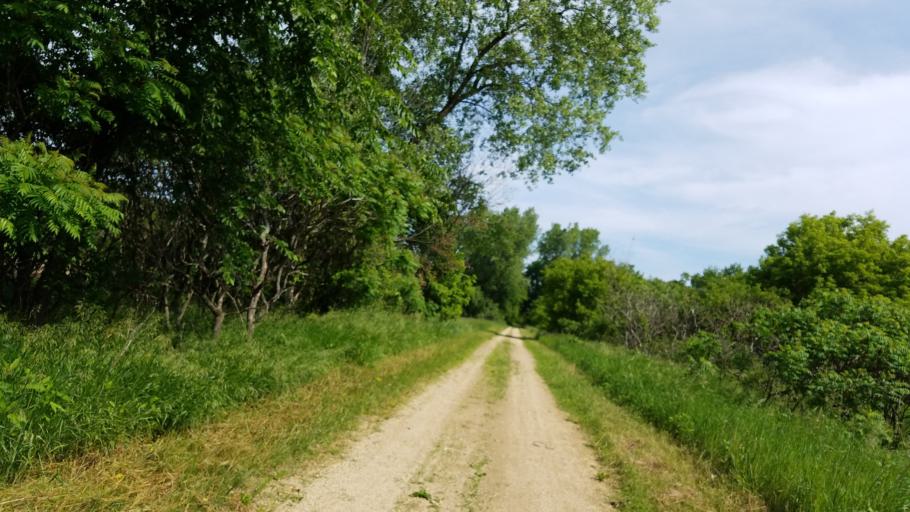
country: US
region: Wisconsin
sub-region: Dunn County
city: Menomonie
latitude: 44.7935
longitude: -91.9471
